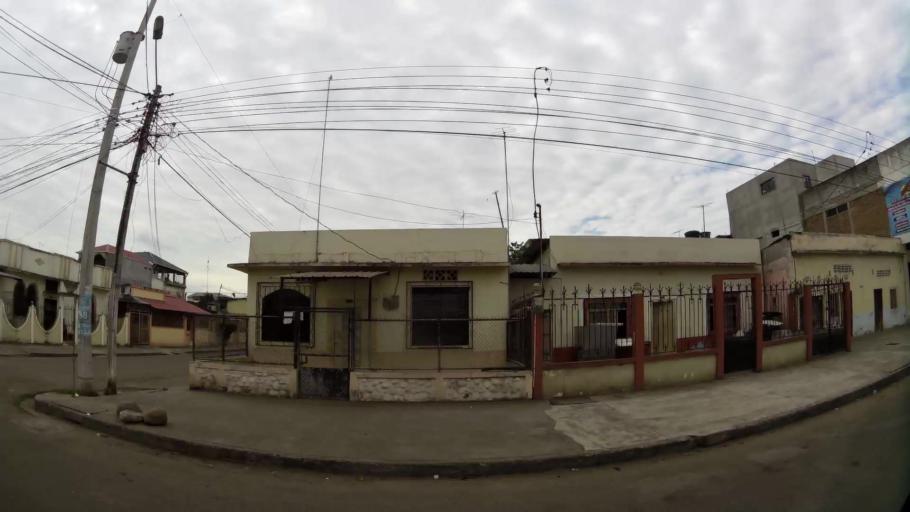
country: EC
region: El Oro
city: Machala
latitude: -3.2535
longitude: -79.9539
